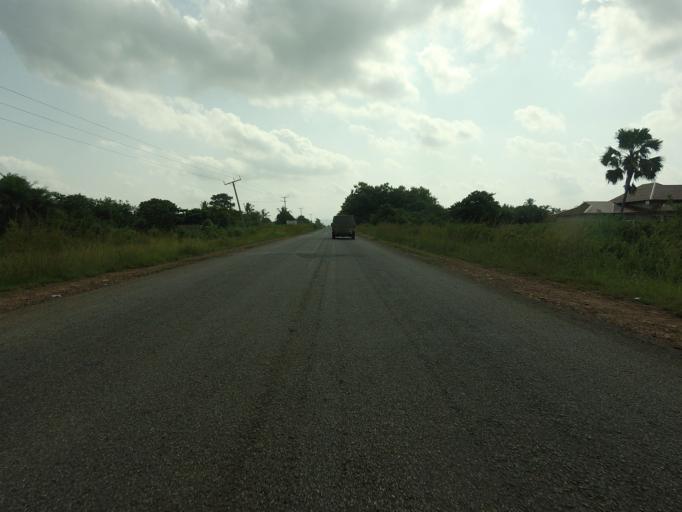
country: GH
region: Volta
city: Ho
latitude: 6.5929
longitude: 0.5463
